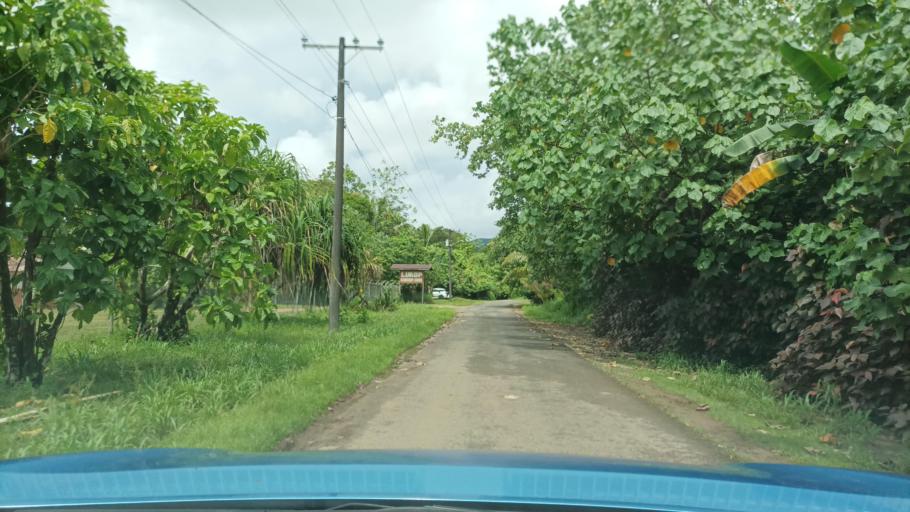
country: FM
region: Pohnpei
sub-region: Madolenihm Municipality
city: Madolenihm Municipality Government
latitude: 6.8861
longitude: 158.3171
